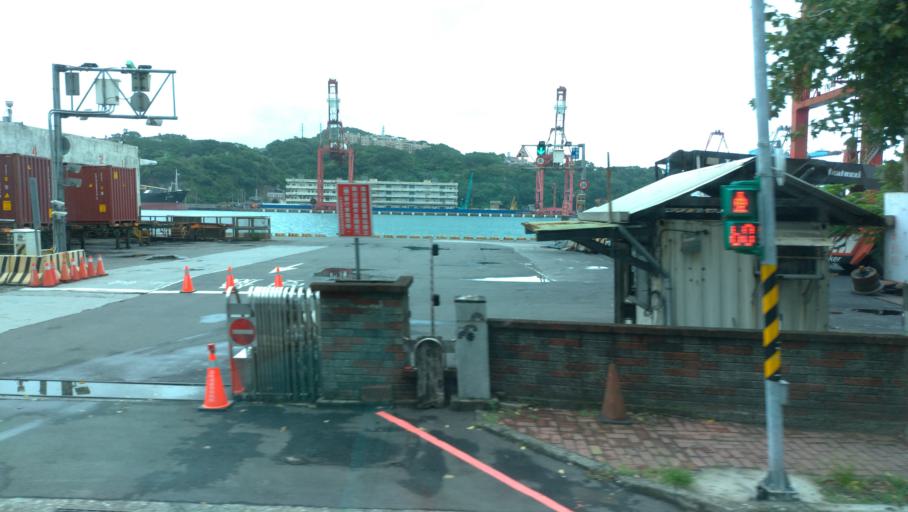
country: TW
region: Taiwan
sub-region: Keelung
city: Keelung
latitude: 25.1387
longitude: 121.7509
